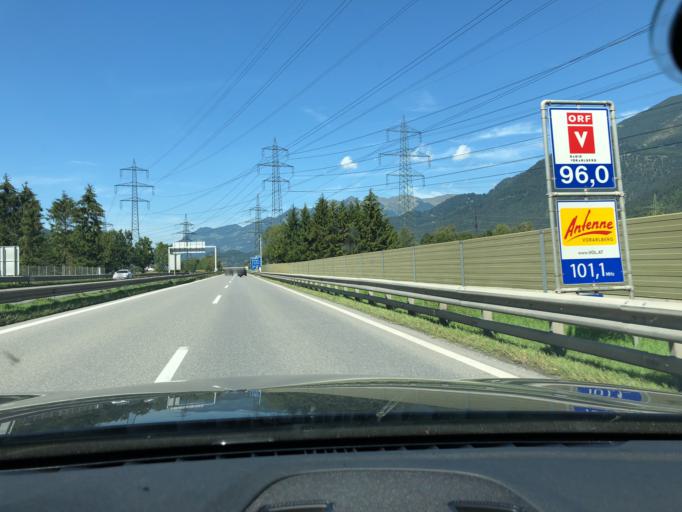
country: AT
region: Vorarlberg
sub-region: Politischer Bezirk Bludenz
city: Bludenz
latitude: 47.1400
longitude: 9.8259
